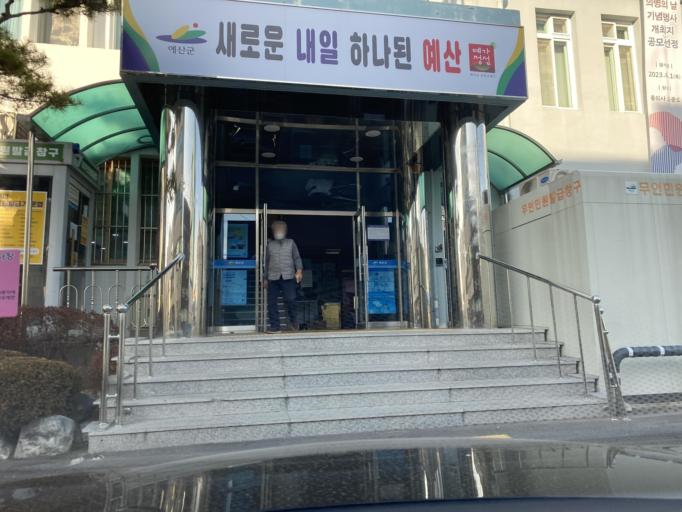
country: KR
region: Chungcheongnam-do
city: Yesan
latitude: 36.6786
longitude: 126.8462
